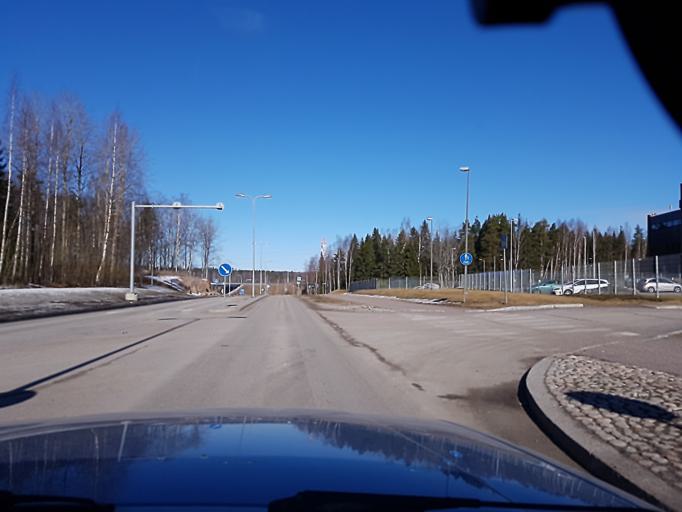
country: FI
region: Uusimaa
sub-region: Helsinki
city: Kilo
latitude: 60.2866
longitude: 24.8511
